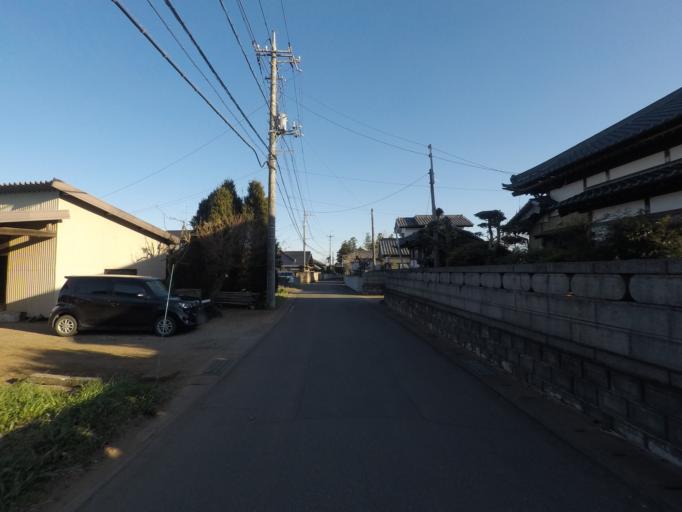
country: JP
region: Ibaraki
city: Ishige
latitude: 36.1073
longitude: 140.0294
